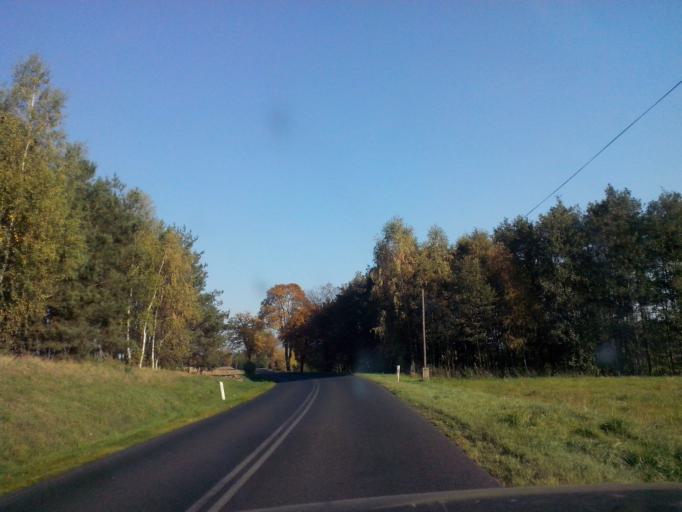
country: PL
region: Kujawsko-Pomorskie
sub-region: Powiat brodnicki
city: Bartniczka
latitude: 53.2466
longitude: 19.6263
